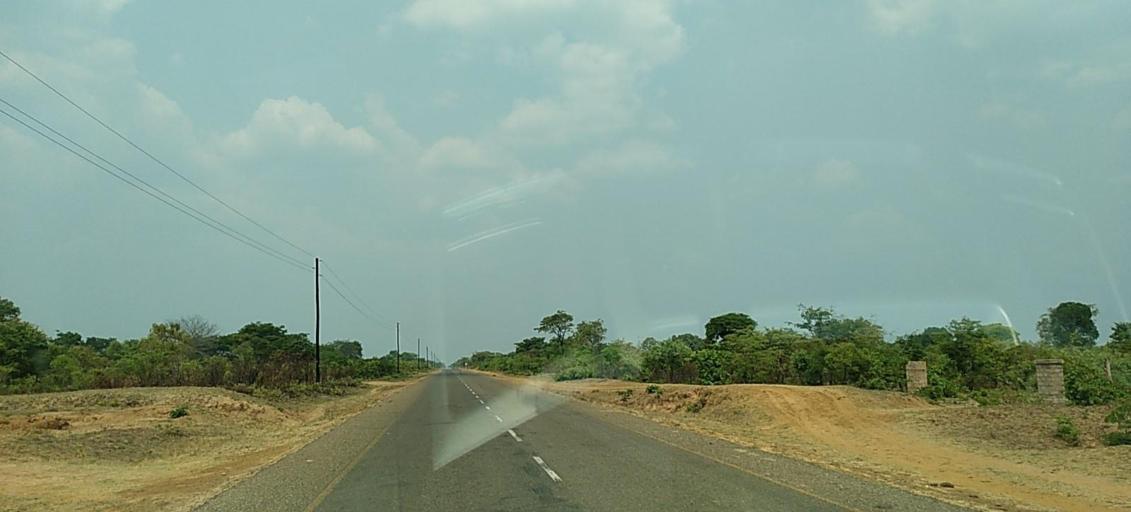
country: ZM
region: North-Western
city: Zambezi
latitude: -13.5517
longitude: 23.1311
